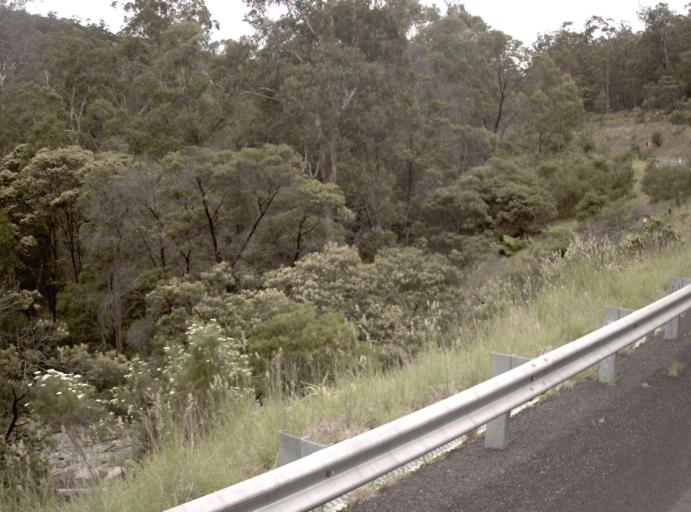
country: AU
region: New South Wales
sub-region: Bombala
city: Bombala
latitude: -37.2503
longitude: 149.2522
